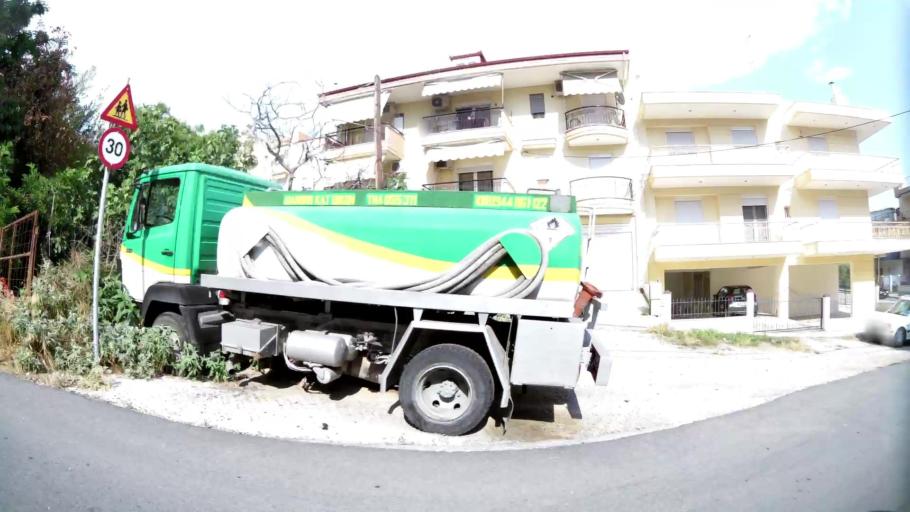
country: GR
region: Central Macedonia
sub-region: Nomos Thessalonikis
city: Sykies
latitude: 40.6575
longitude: 22.9621
